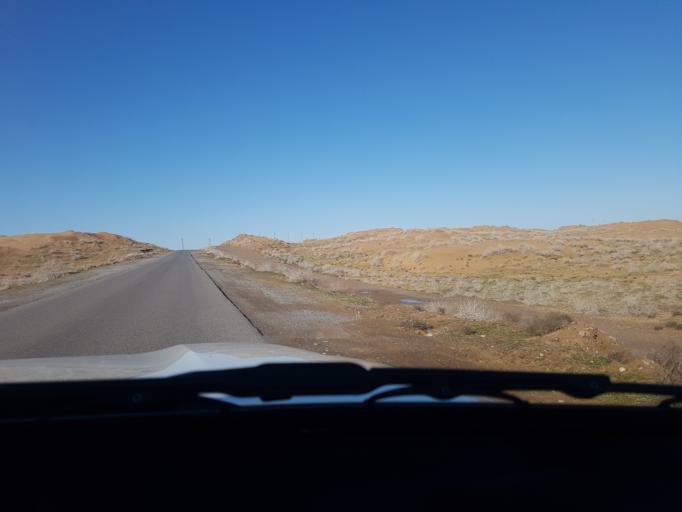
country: TM
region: Mary
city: Yoloeten
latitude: 37.0385
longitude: 62.4517
